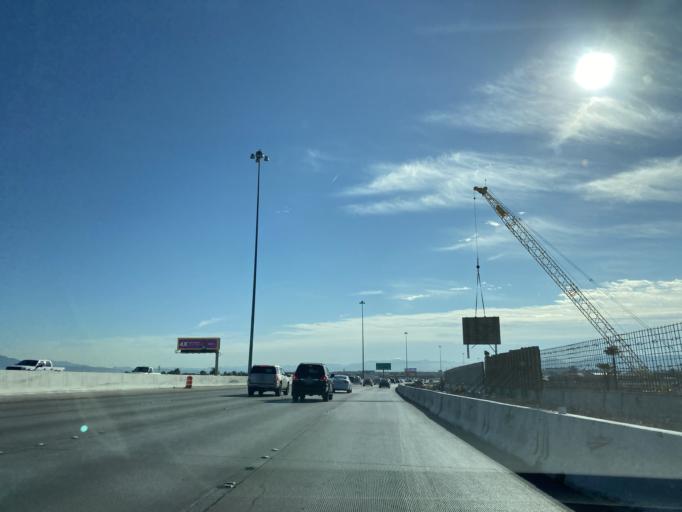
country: US
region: Nevada
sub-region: Clark County
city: Spring Valley
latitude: 36.0684
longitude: -115.1999
